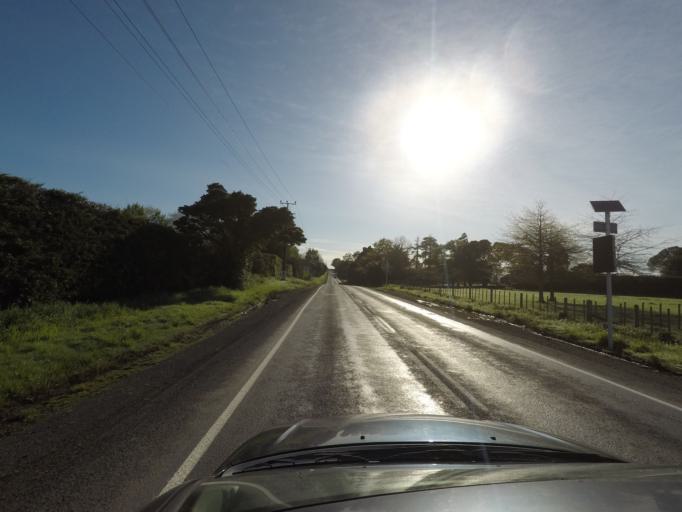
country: NZ
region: Auckland
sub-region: Auckland
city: Papakura
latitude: -37.0155
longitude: 174.9422
